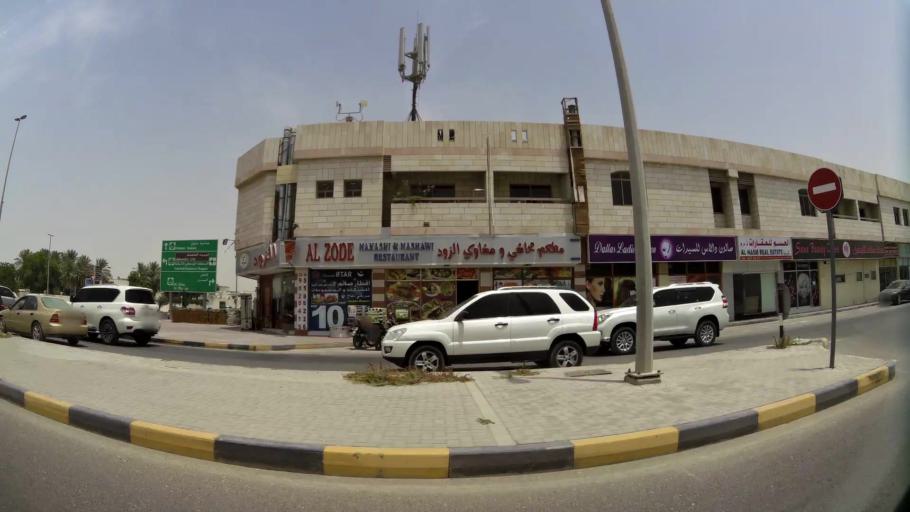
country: AE
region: Ash Shariqah
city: Sharjah
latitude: 25.3541
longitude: 55.4081
